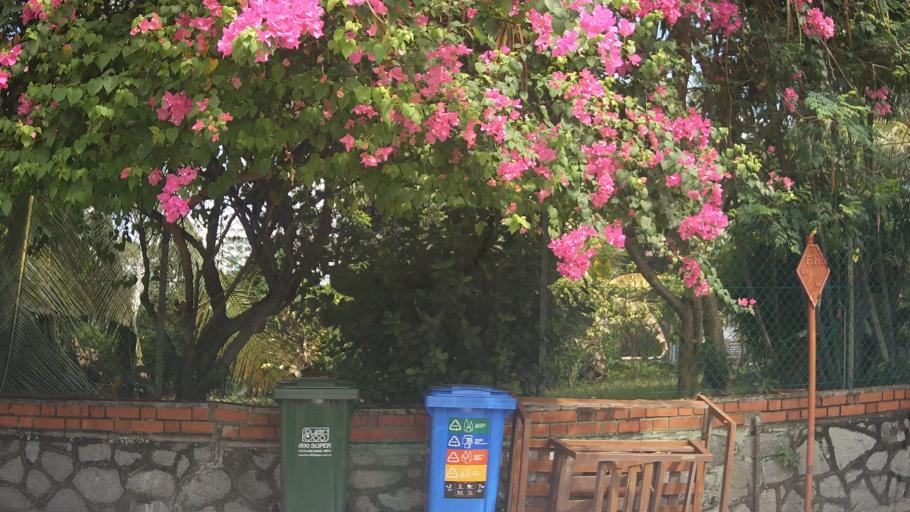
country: SG
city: Singapore
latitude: 1.3257
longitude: 103.9479
